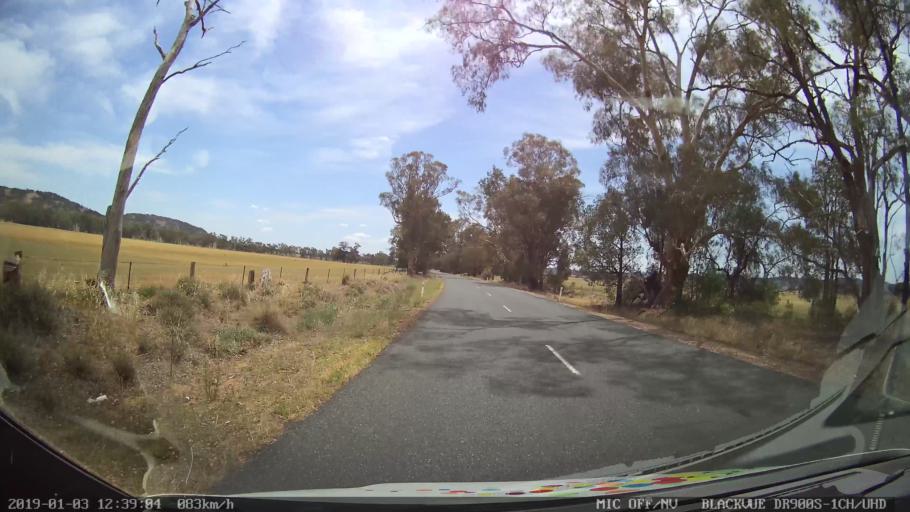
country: AU
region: New South Wales
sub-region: Weddin
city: Grenfell
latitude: -33.8282
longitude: 148.2028
